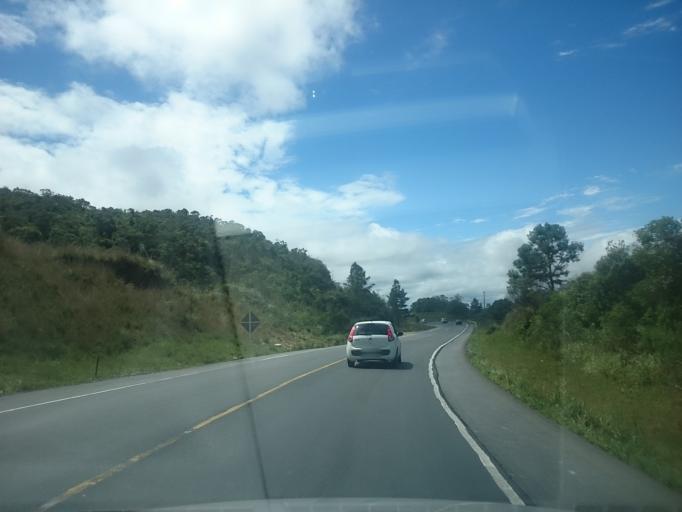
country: BR
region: Santa Catarina
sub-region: Anitapolis
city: Anitapolis
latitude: -27.6658
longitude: -49.1603
